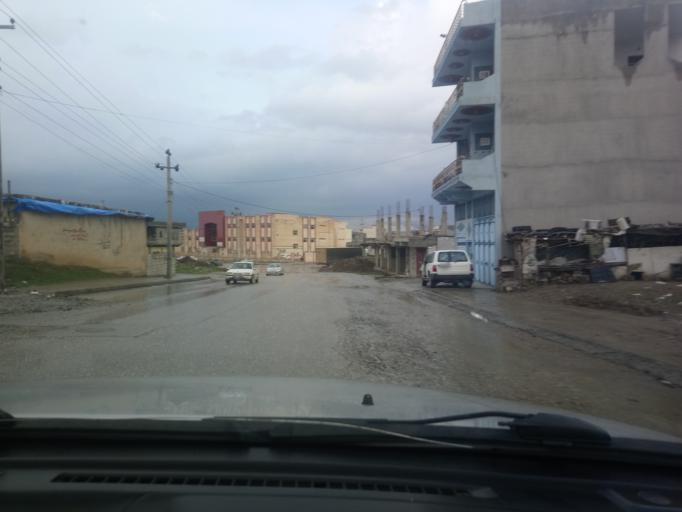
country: IQ
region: As Sulaymaniyah
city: Qeladize
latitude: 36.1806
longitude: 45.1376
